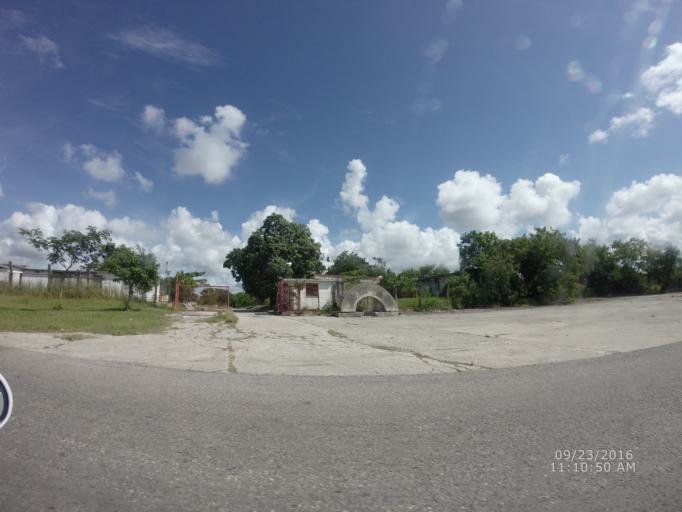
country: CU
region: La Habana
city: Arroyo Naranjo
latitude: 23.0228
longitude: -82.2609
